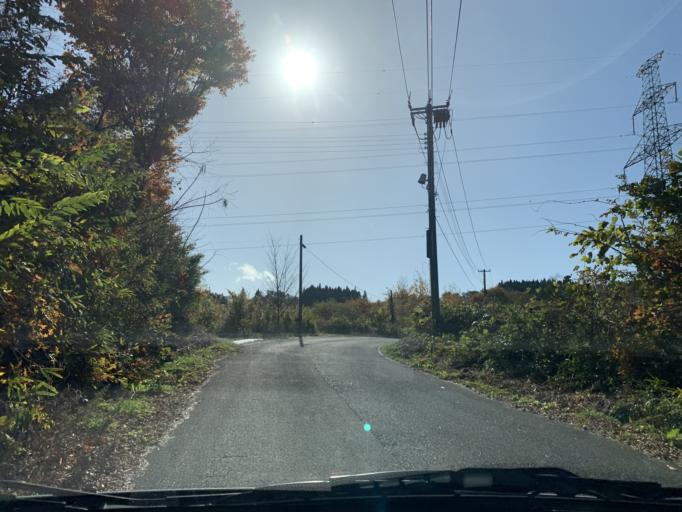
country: JP
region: Iwate
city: Mizusawa
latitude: 39.0272
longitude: 141.1038
